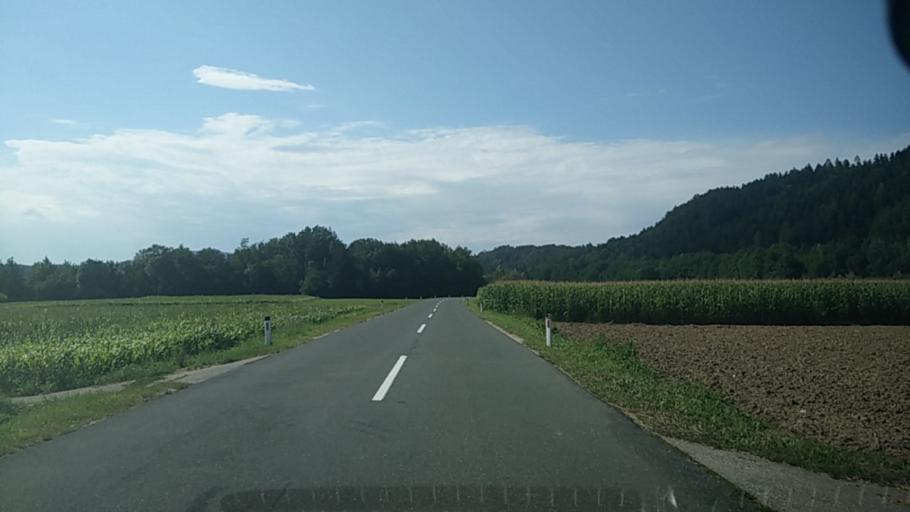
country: AT
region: Carinthia
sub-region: Politischer Bezirk Volkermarkt
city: Sittersdorf
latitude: 46.5525
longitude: 14.5797
